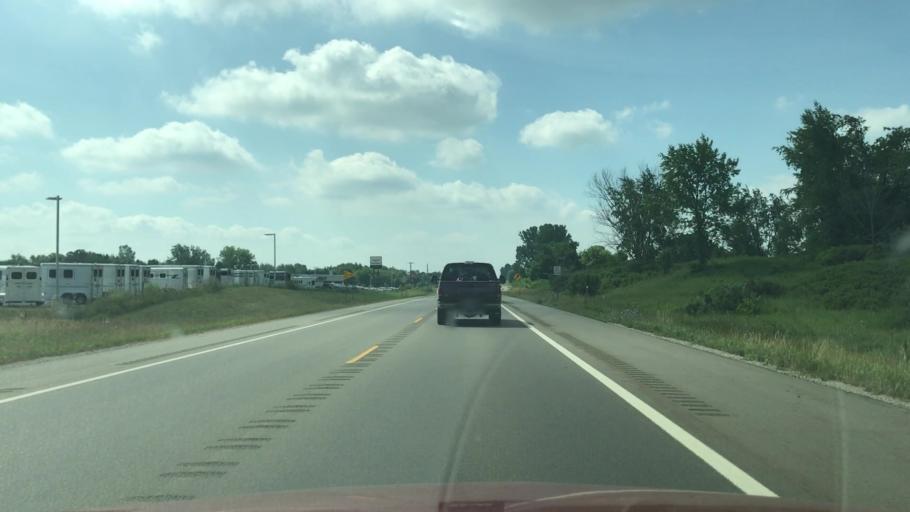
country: US
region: Michigan
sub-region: Kent County
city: Sparta
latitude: 43.1294
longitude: -85.7130
